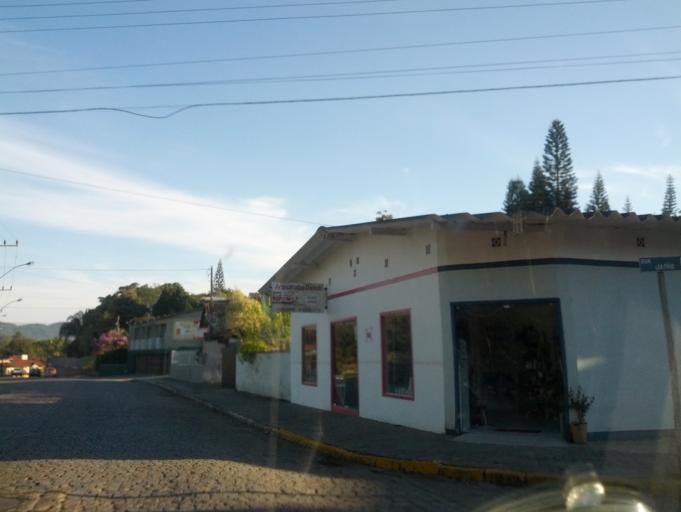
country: BR
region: Santa Catarina
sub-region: Indaial
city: Indaial
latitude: -26.8937
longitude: -49.2429
